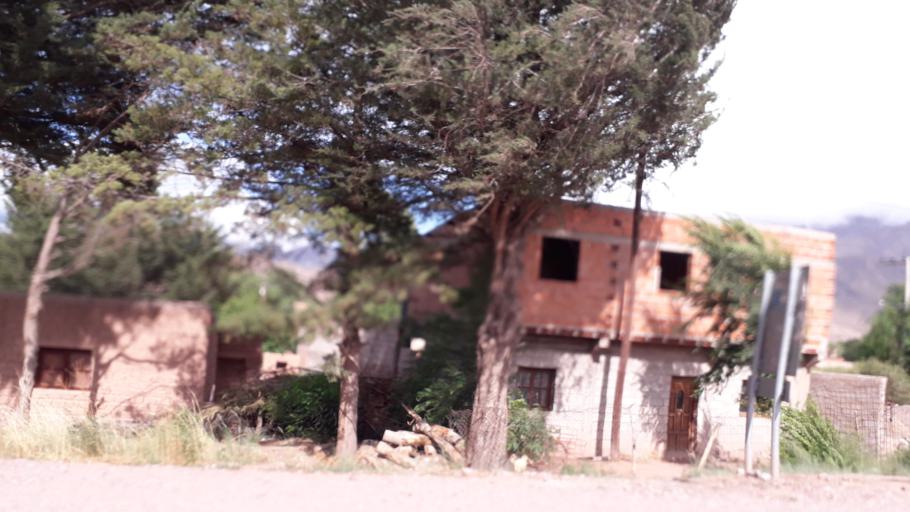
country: AR
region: Jujuy
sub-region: Departamento de Humahuaca
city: Humahuaca
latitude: -23.3057
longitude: -65.3547
